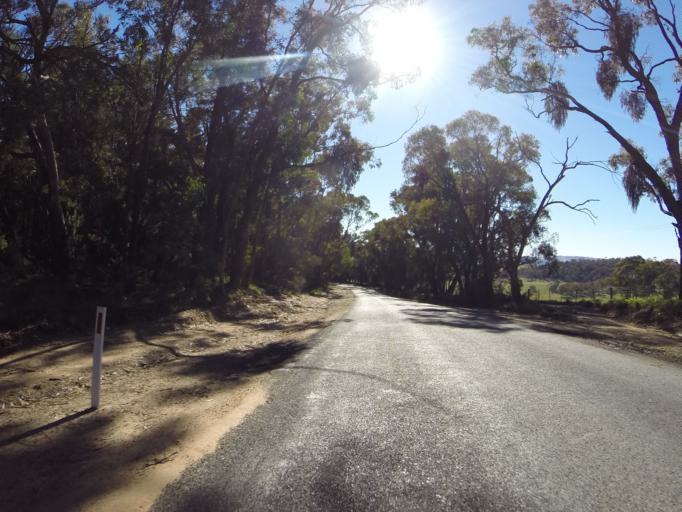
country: AU
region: New South Wales
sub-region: Oberon
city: Oberon
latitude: -33.6152
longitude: 149.8486
